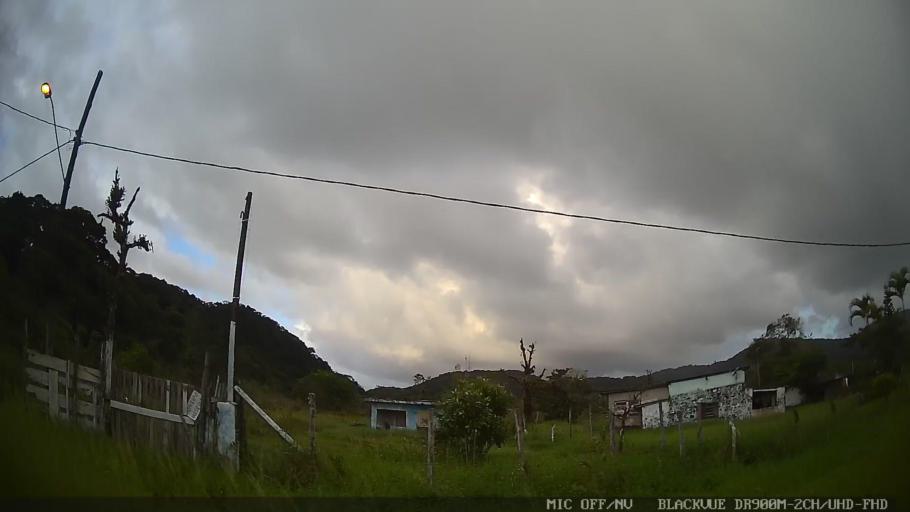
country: BR
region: Sao Paulo
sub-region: Itanhaem
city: Itanhaem
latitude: -24.1267
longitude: -46.7815
